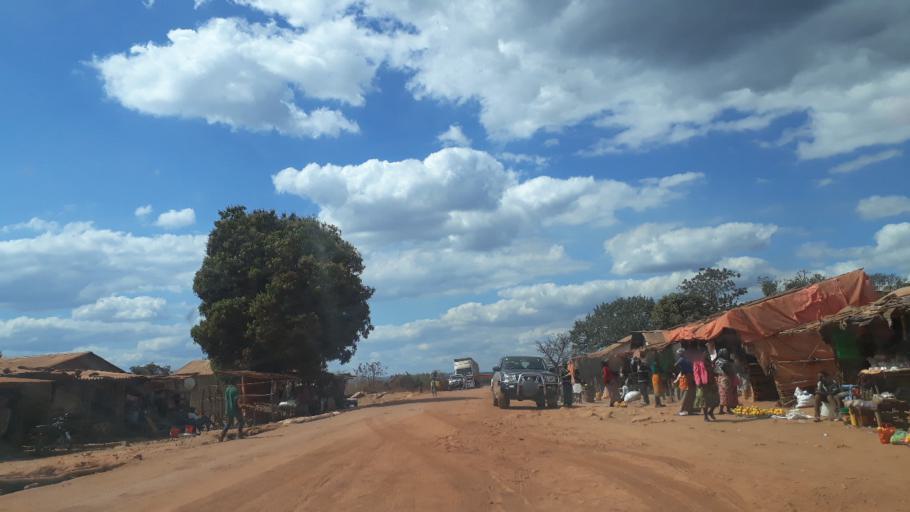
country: ZM
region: Copperbelt
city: Mufulira
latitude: -11.9978
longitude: 28.7225
